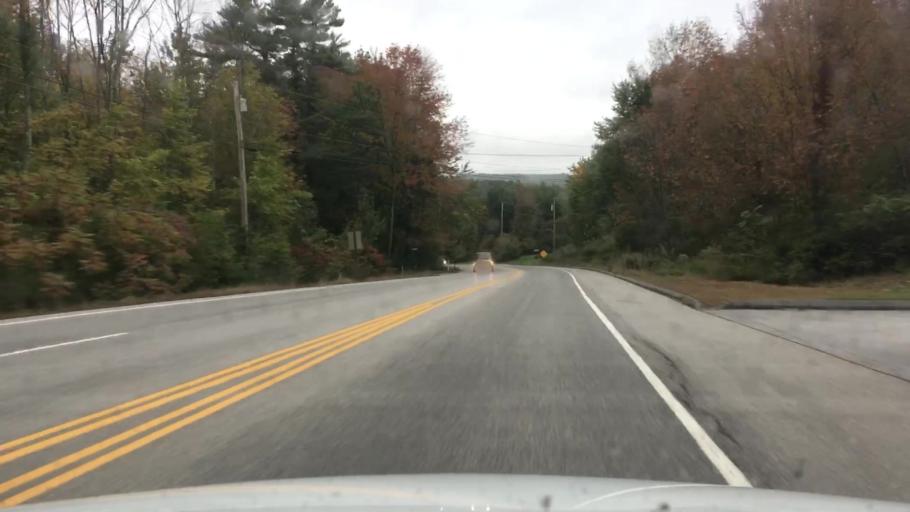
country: US
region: Maine
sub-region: Androscoggin County
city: Poland
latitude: 44.0343
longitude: -70.3690
